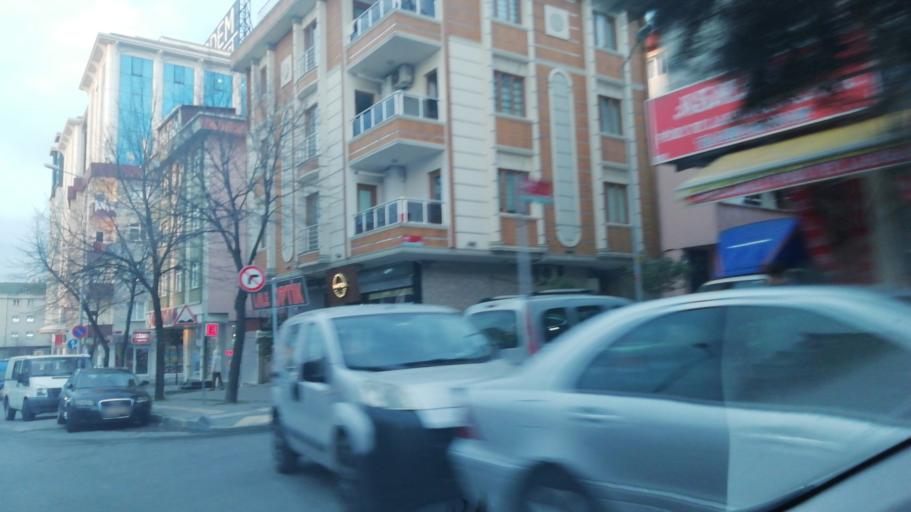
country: TR
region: Istanbul
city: Mahmutbey
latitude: 41.0392
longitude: 28.8251
